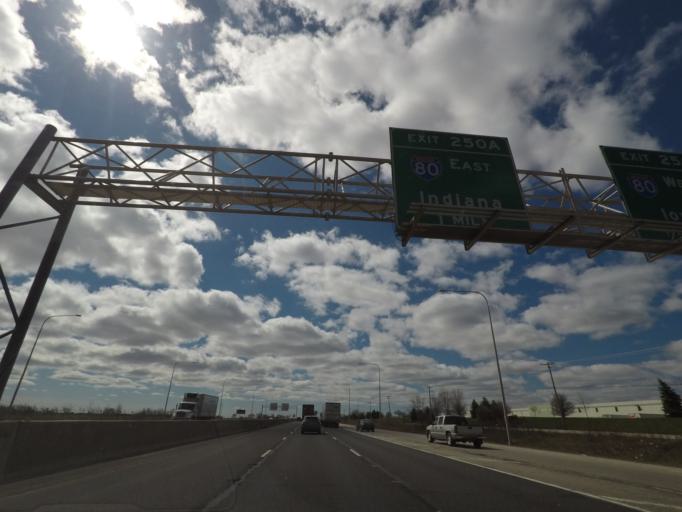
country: US
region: Illinois
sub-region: Will County
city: Shorewood
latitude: 41.4992
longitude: -88.1980
